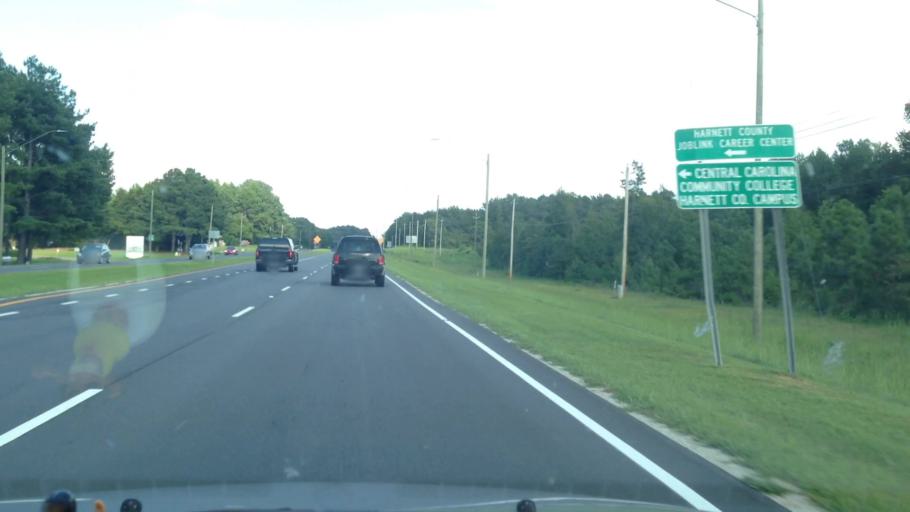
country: US
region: North Carolina
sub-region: Harnett County
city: Lillington
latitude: 35.4107
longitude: -78.7870
